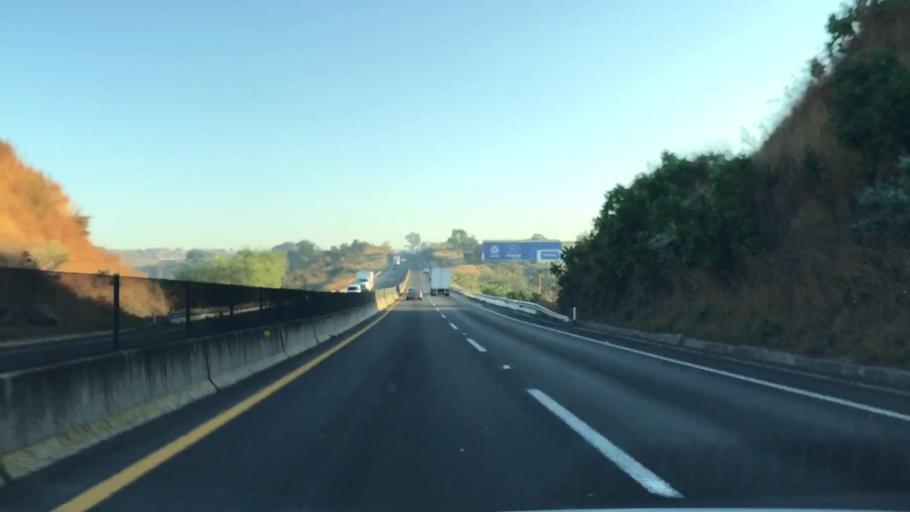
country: MX
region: Jalisco
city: Tepatitlan de Morelos
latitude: 20.8053
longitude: -102.8101
